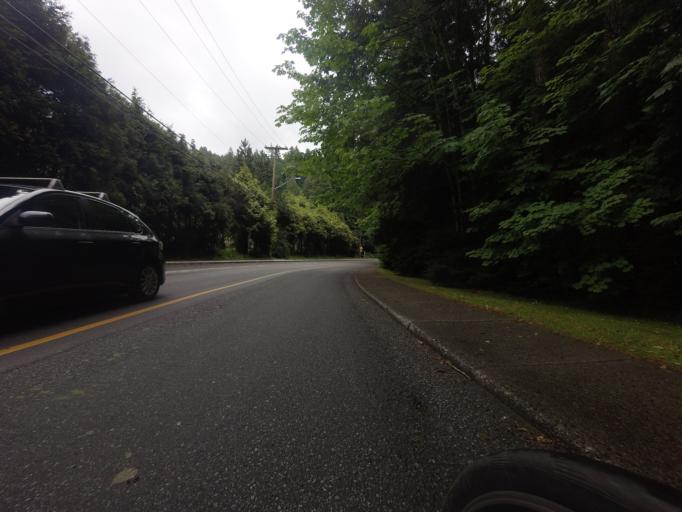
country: CA
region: British Columbia
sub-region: Greater Vancouver Regional District
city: Bowen Island
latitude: 49.3536
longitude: -123.2615
